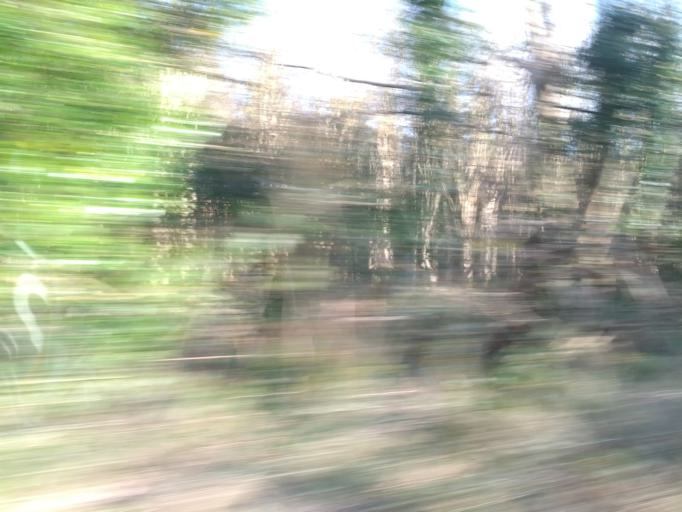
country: IE
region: Connaught
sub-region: County Galway
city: Athenry
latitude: 53.3911
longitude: -8.5825
